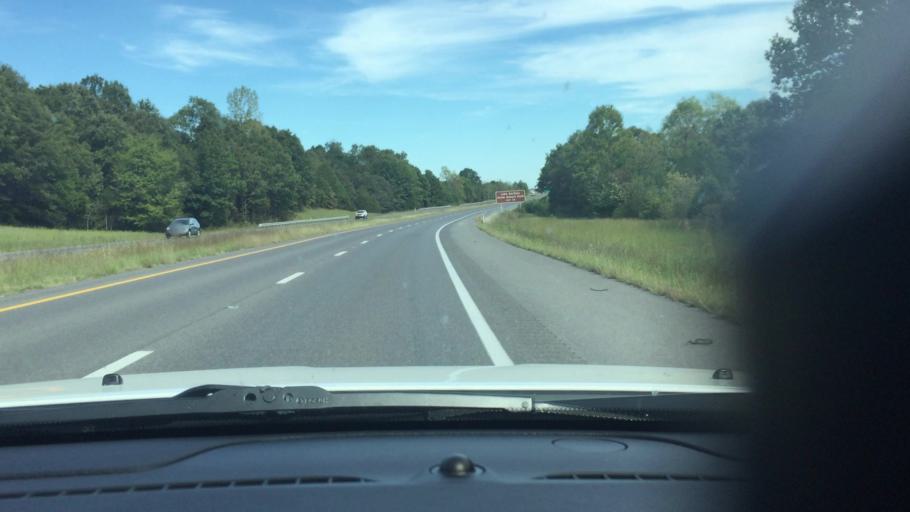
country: US
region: Kentucky
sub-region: Caldwell County
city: Princeton
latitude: 37.1171
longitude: -87.9217
